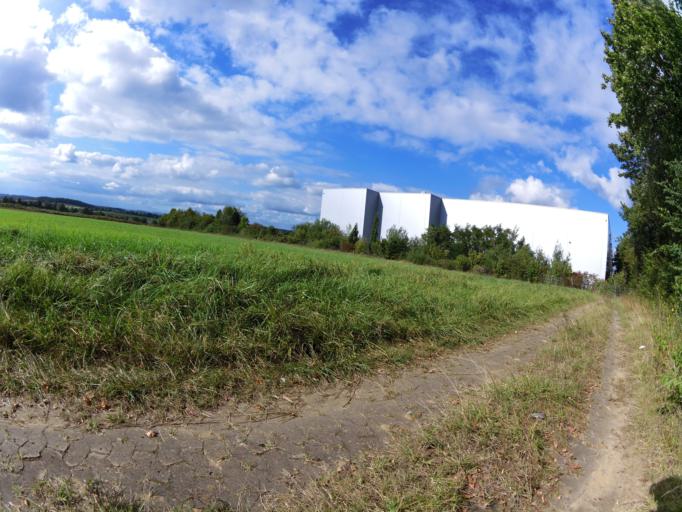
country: DE
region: Bavaria
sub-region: Regierungsbezirk Unterfranken
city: Waldbuttelbrunn
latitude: 49.7924
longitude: 9.8429
